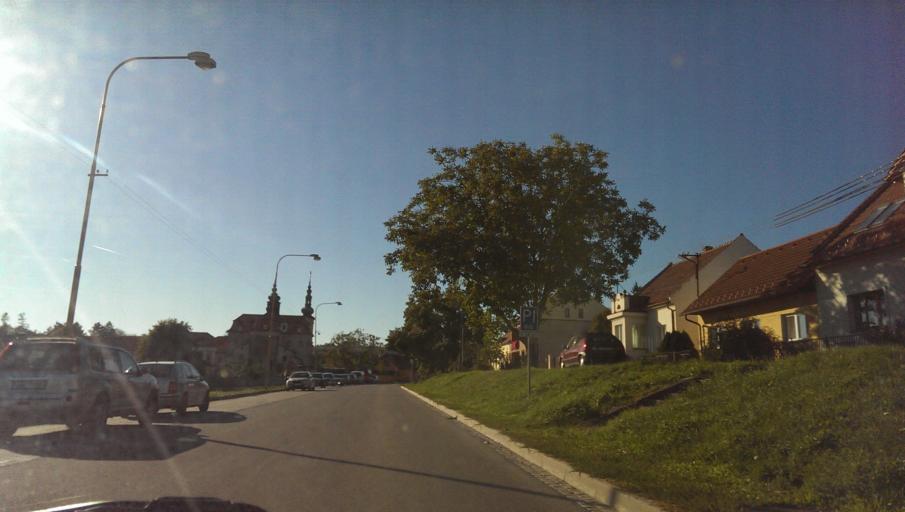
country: CZ
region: Zlin
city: Velehrad
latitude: 49.1035
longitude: 17.3999
